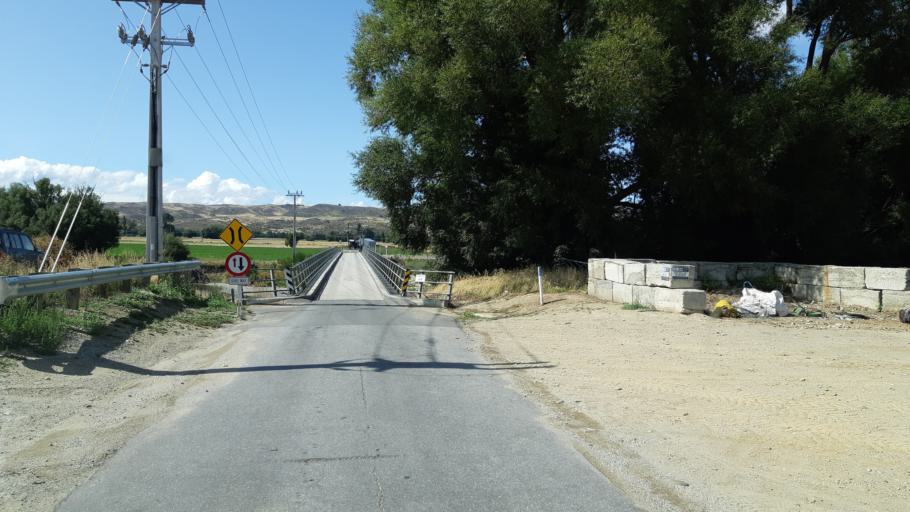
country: NZ
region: Otago
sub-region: Queenstown-Lakes District
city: Wanaka
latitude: -45.0947
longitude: 169.6019
